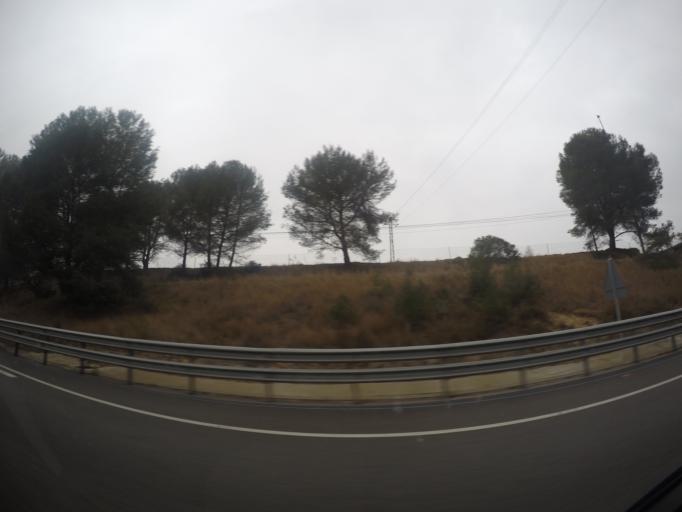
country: ES
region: Catalonia
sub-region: Provincia de Barcelona
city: Gelida
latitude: 41.4452
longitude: 1.8604
